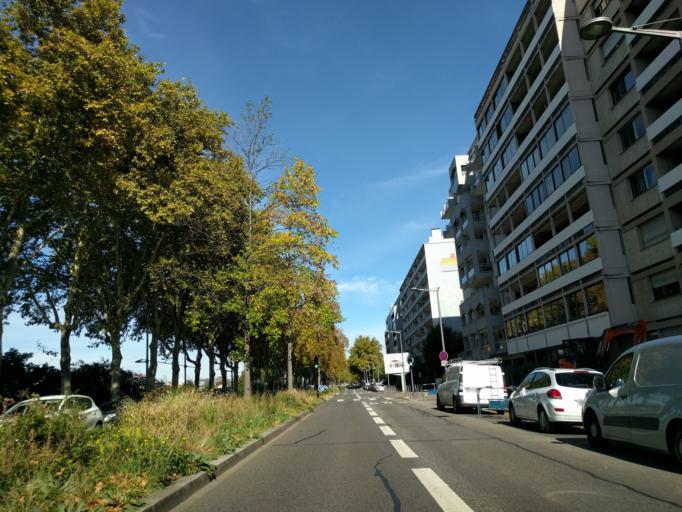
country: FR
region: Rhone-Alpes
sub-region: Departement du Rhone
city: La Mulatiere
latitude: 45.7379
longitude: 4.8250
